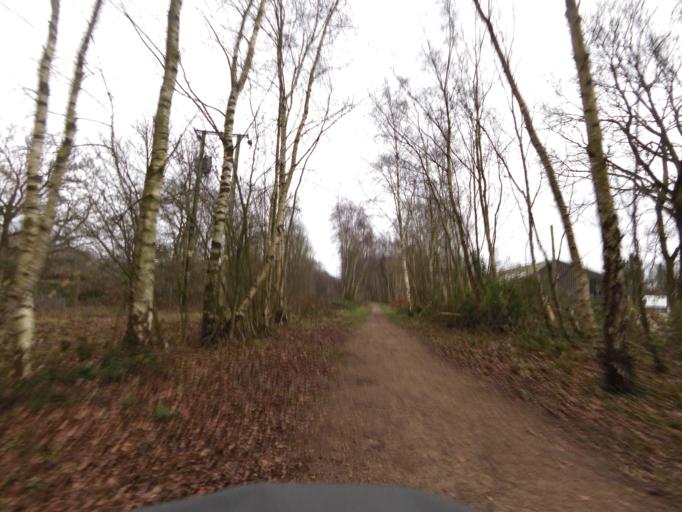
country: GB
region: England
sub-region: Norfolk
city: Mattishall
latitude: 52.7220
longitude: 1.1173
